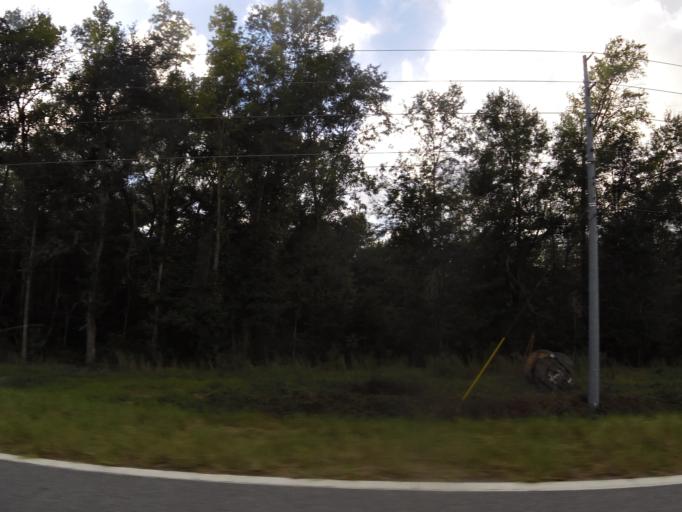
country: US
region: Georgia
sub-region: Liberty County
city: Midway
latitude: 31.7698
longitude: -81.4487
